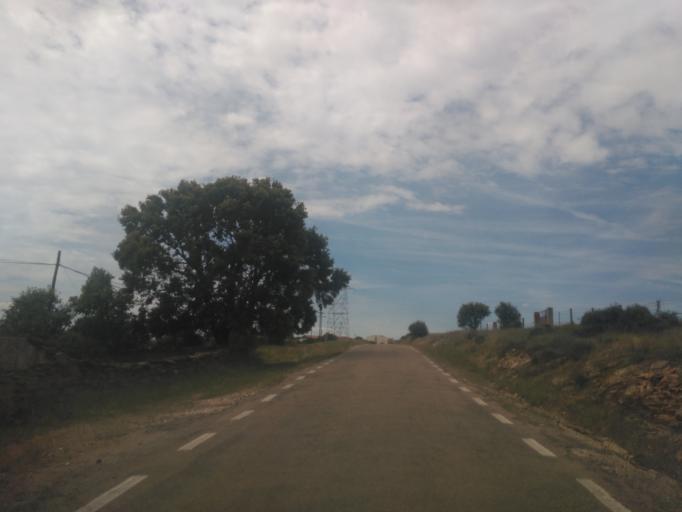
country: ES
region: Castille and Leon
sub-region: Provincia de Salamanca
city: Guijuelo
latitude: 40.5463
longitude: -5.6644
